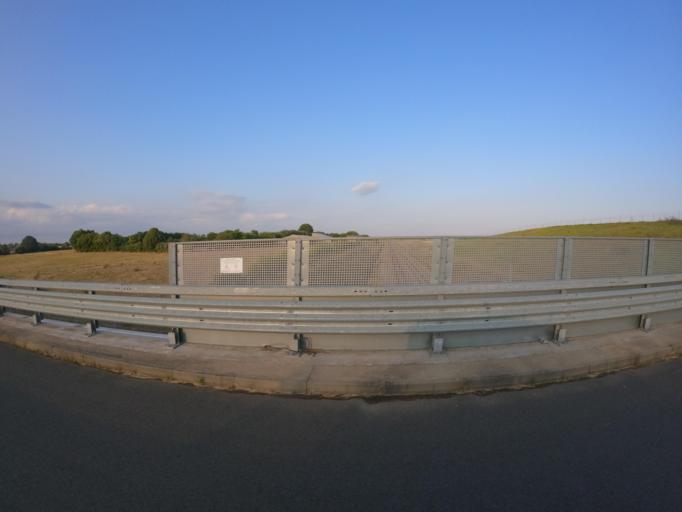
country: FR
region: Pays de la Loire
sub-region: Departement de la Sarthe
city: Brulon
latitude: 47.9101
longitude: -0.2292
